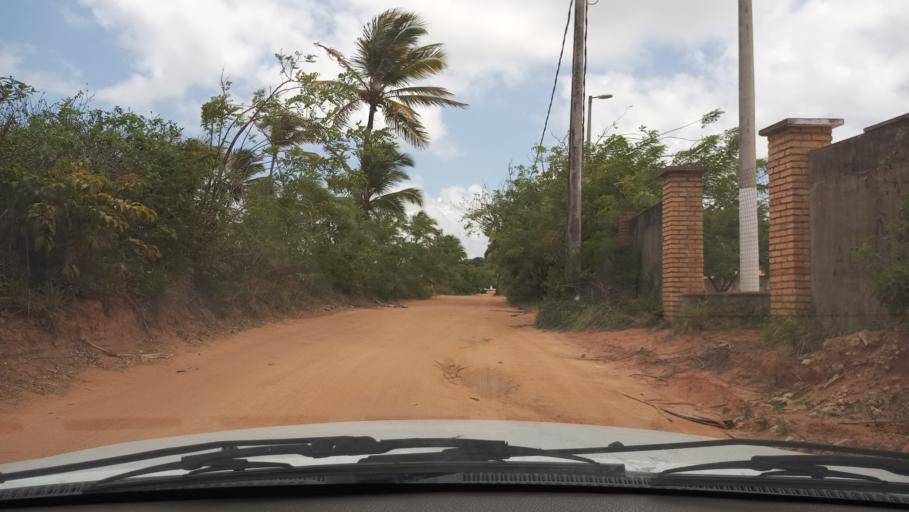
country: BR
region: Rio Grande do Norte
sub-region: Ares
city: Ares
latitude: -6.2365
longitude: -35.0388
